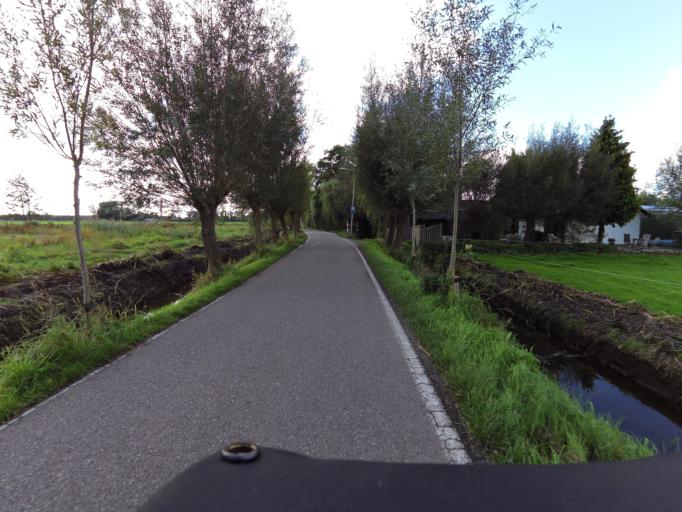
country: NL
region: South Holland
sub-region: Gemeente Vlaardingen
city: Vlaardingen
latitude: 51.9547
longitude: 4.3472
